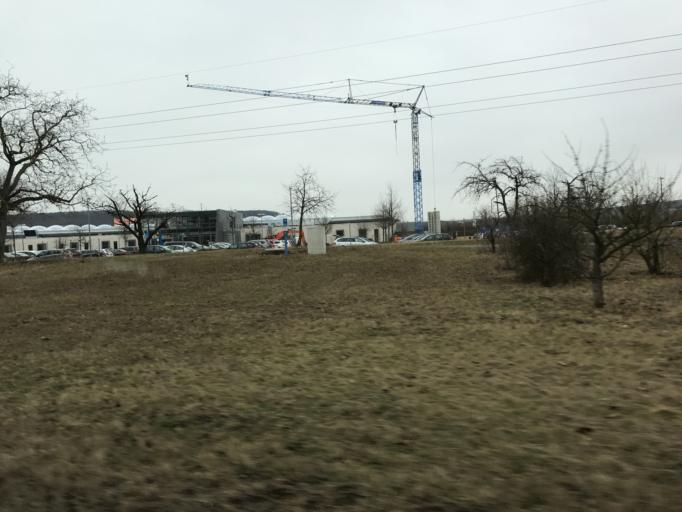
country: DE
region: Rheinland-Pfalz
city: Gau-Algesheim
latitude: 49.9693
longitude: 8.0031
